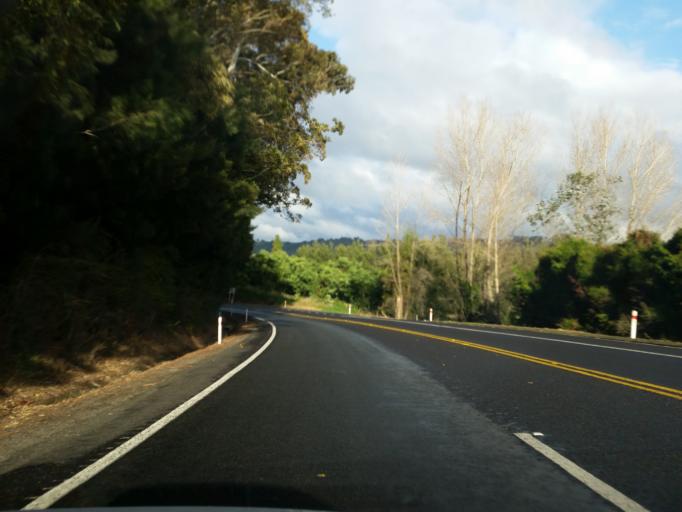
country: NZ
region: Bay of Plenty
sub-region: Tauranga City
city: Tauranga
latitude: -37.6816
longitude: 176.0259
